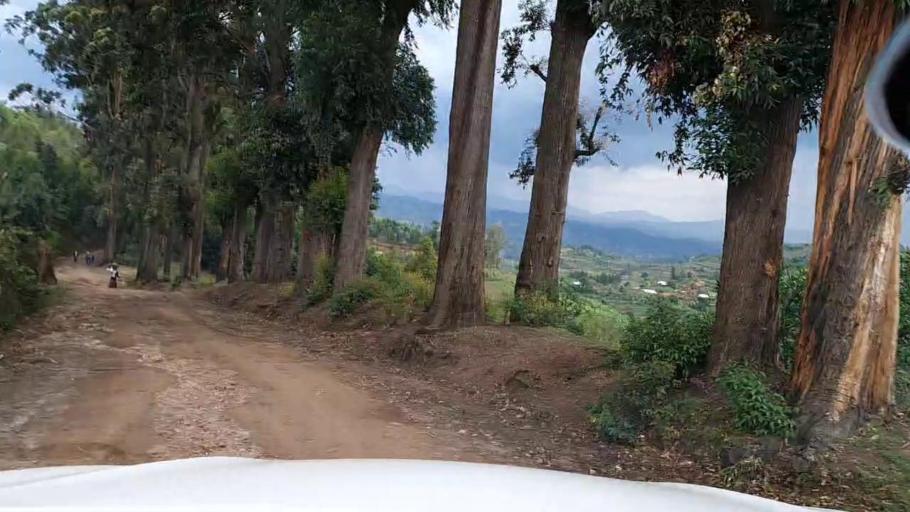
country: BI
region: Kayanza
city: Kayanza
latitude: -2.7958
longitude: 29.5167
